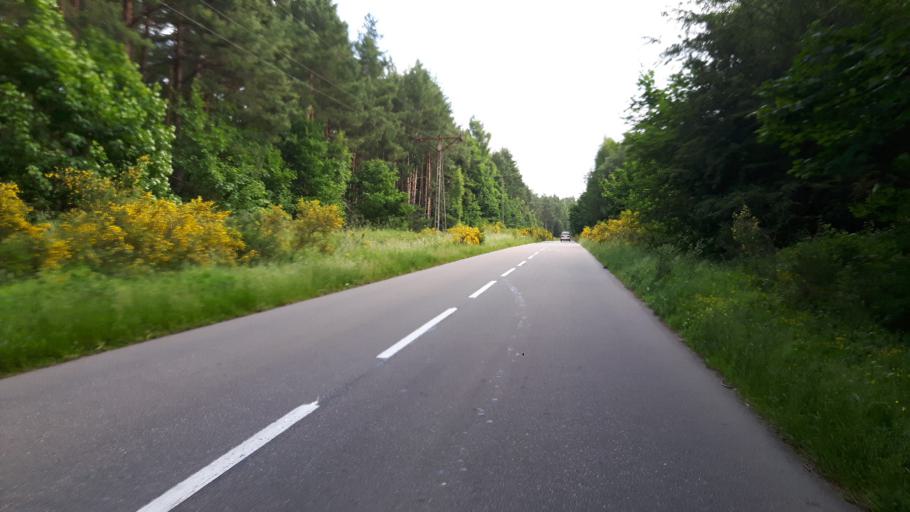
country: PL
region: Pomeranian Voivodeship
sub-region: Powiat leborski
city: Leba
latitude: 54.7463
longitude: 17.7216
